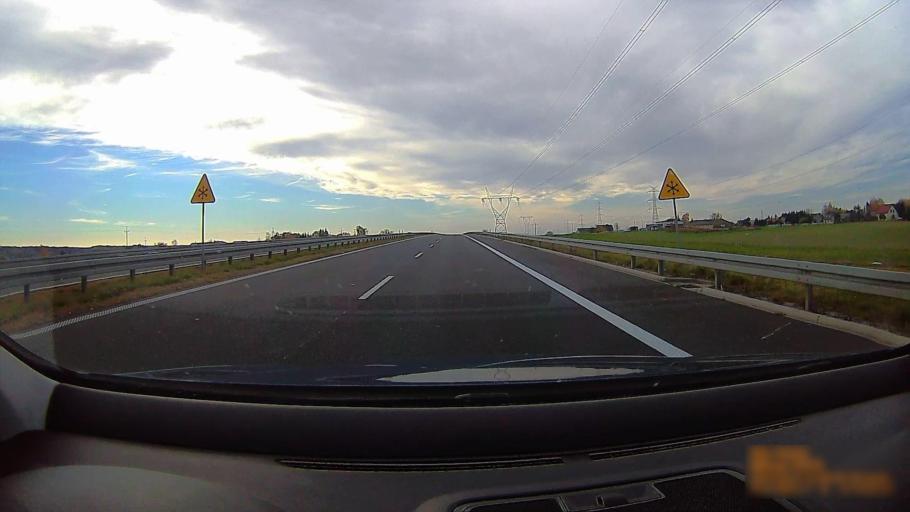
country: PL
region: Greater Poland Voivodeship
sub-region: Powiat ostrowski
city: Przygodzice
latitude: 51.6083
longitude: 17.8557
